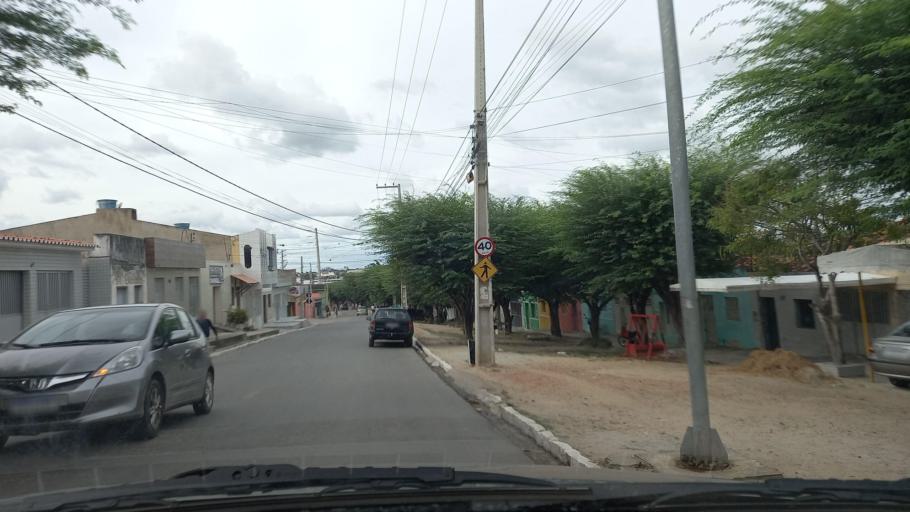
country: BR
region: Pernambuco
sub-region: Gravata
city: Gravata
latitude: -8.2083
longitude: -35.5704
